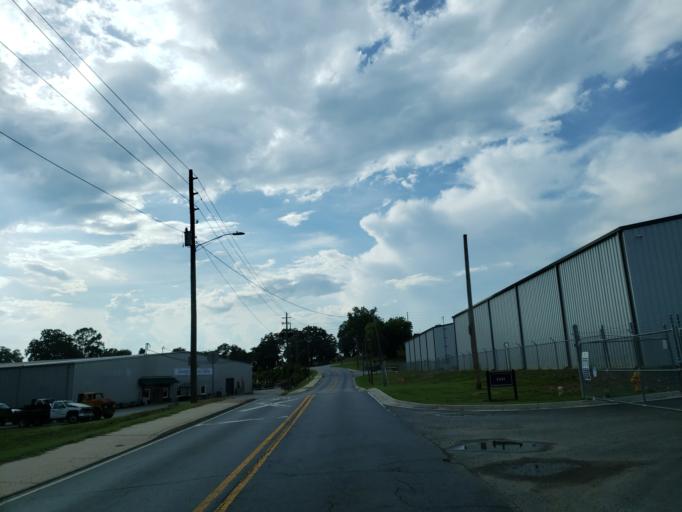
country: US
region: Georgia
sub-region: Bartow County
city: Cartersville
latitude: 34.1753
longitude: -84.8035
